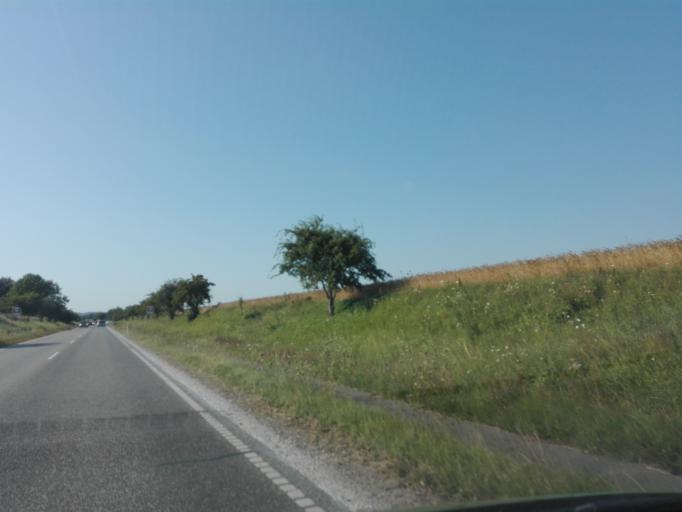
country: DK
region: Central Jutland
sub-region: Odder Kommune
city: Odder
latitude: 55.9545
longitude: 10.1946
